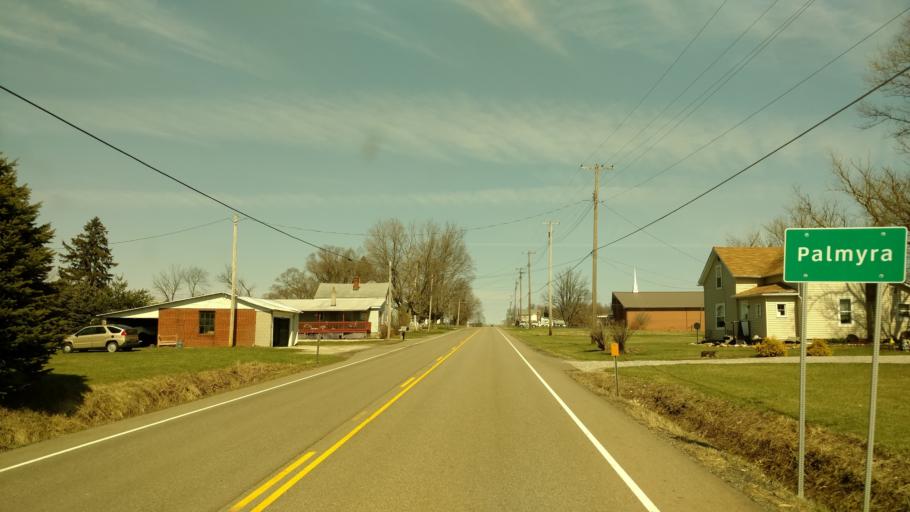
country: US
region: Ohio
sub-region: Knox County
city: Fredericktown
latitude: 40.5430
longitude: -82.5420
